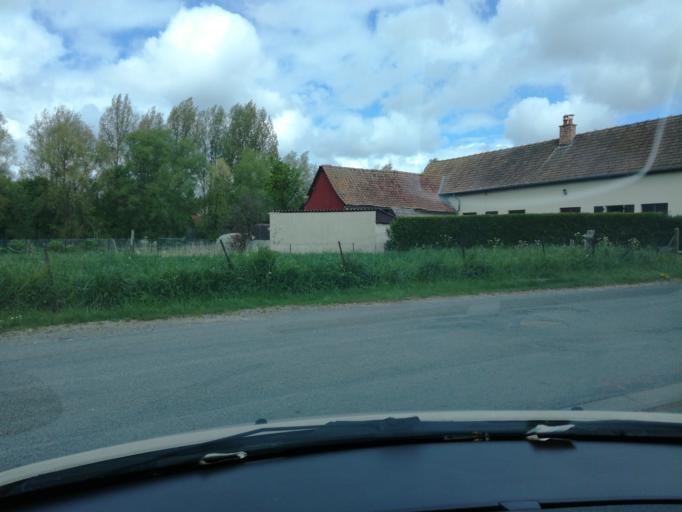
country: FR
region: Picardie
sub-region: Departement de la Somme
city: Pont-Remy
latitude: 50.0638
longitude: 1.8829
